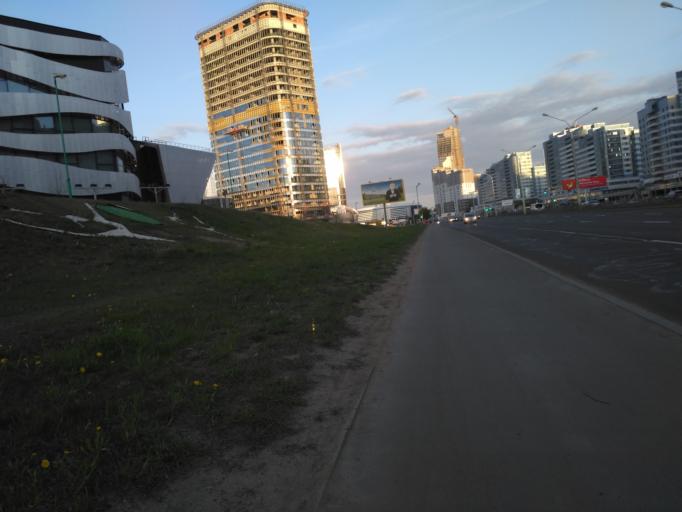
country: BY
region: Minsk
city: Zhdanovichy
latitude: 53.9419
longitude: 27.4669
